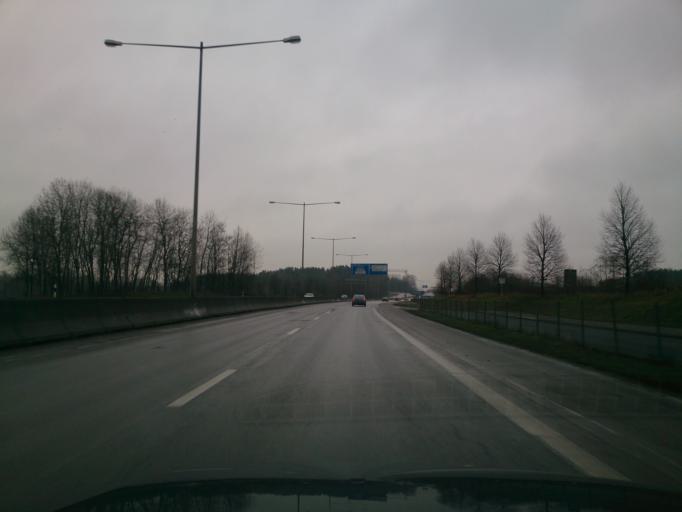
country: SE
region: OEstergoetland
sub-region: Norrkopings Kommun
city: Norrkoping
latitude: 58.5802
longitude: 16.1262
